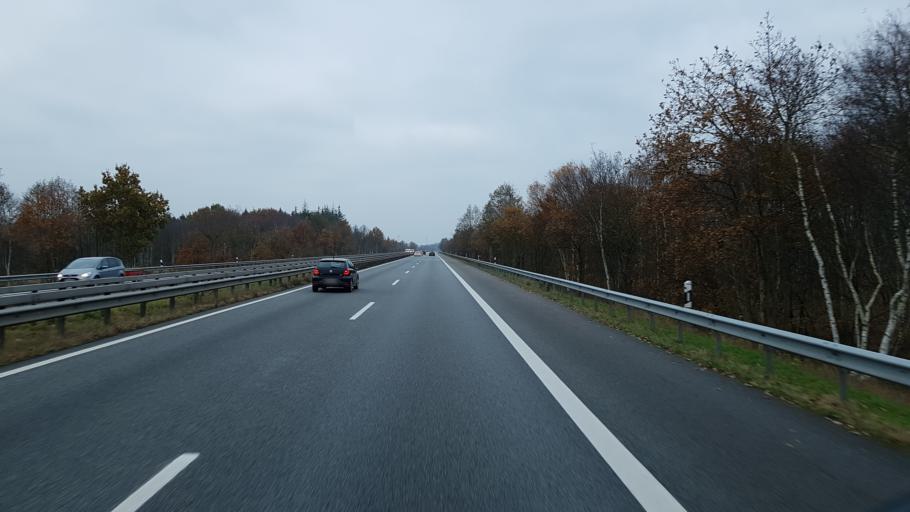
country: DE
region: Lower Saxony
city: Driftsethe
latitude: 53.4176
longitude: 8.5807
